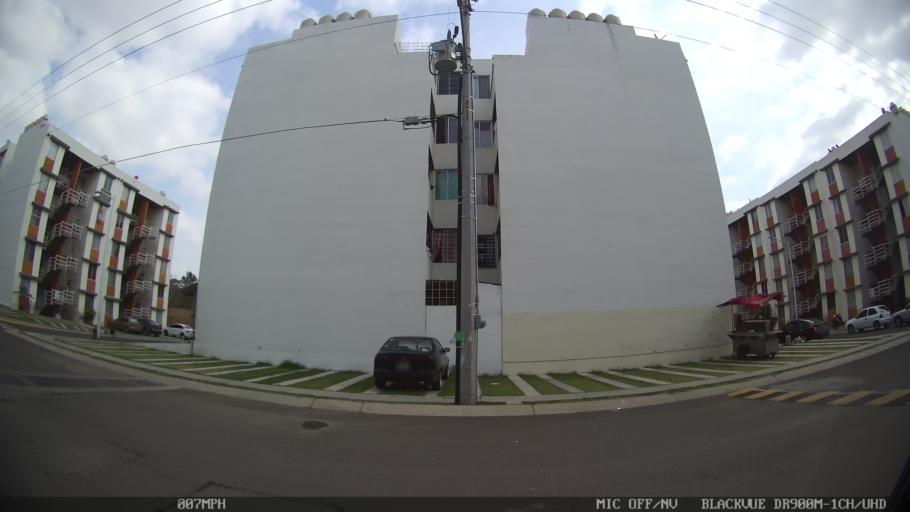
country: MX
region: Jalisco
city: Tonala
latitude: 20.6333
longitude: -103.2203
